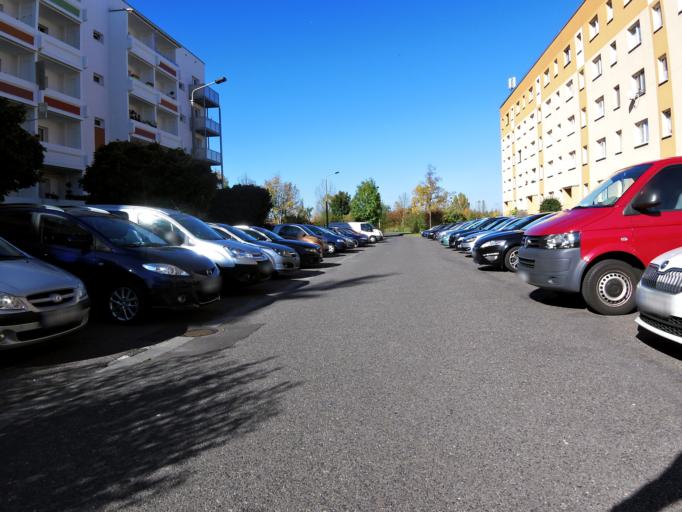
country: DE
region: Saxony
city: Leipzig
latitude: 51.3804
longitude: 12.3616
